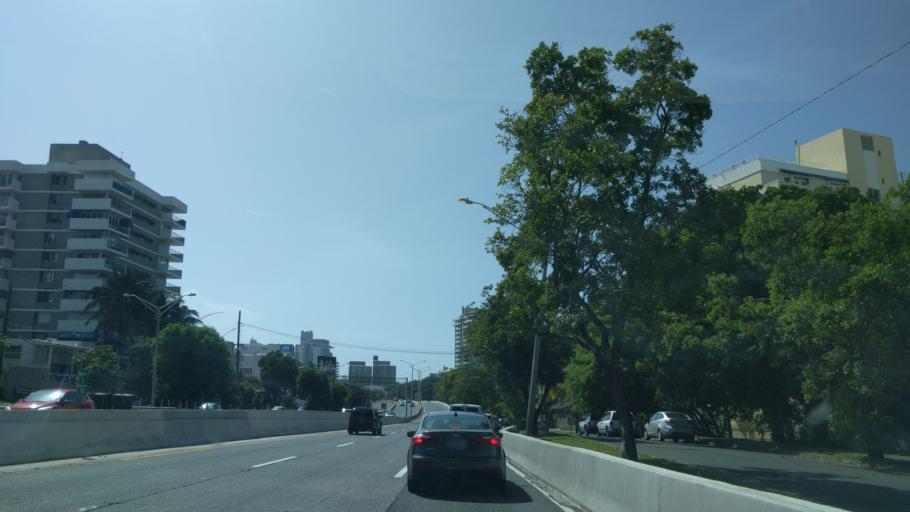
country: PR
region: San Juan
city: San Juan
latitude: 18.4521
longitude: -66.0704
